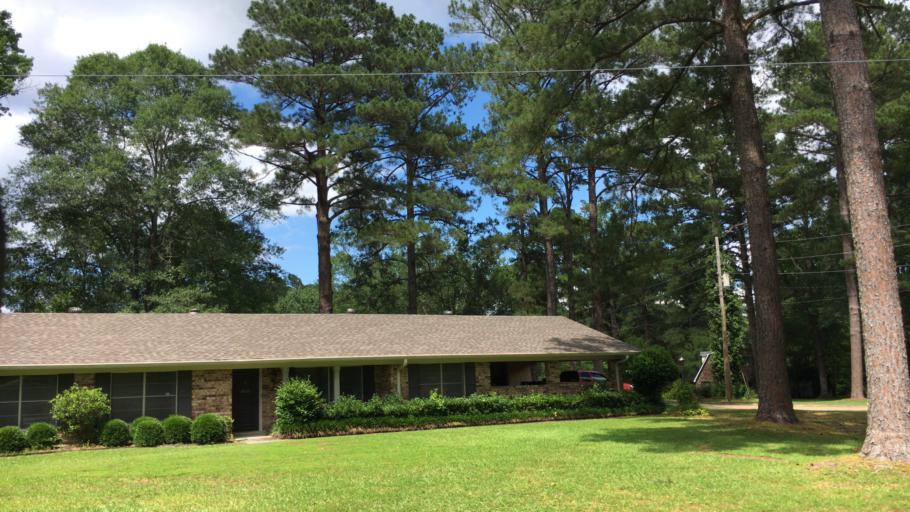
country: US
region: Louisiana
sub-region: Lincoln Parish
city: Ruston
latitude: 32.5485
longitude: -92.6382
